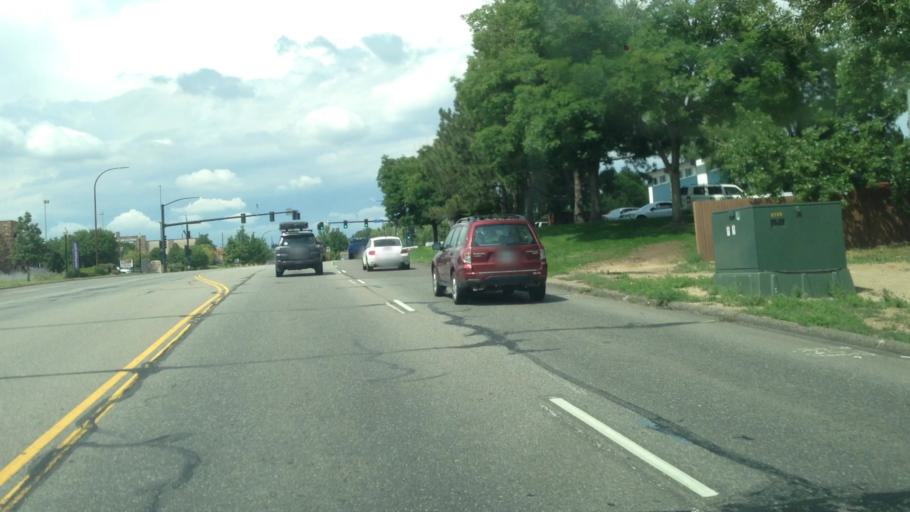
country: US
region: Colorado
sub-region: Jefferson County
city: Arvada
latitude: 39.7889
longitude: -105.1095
